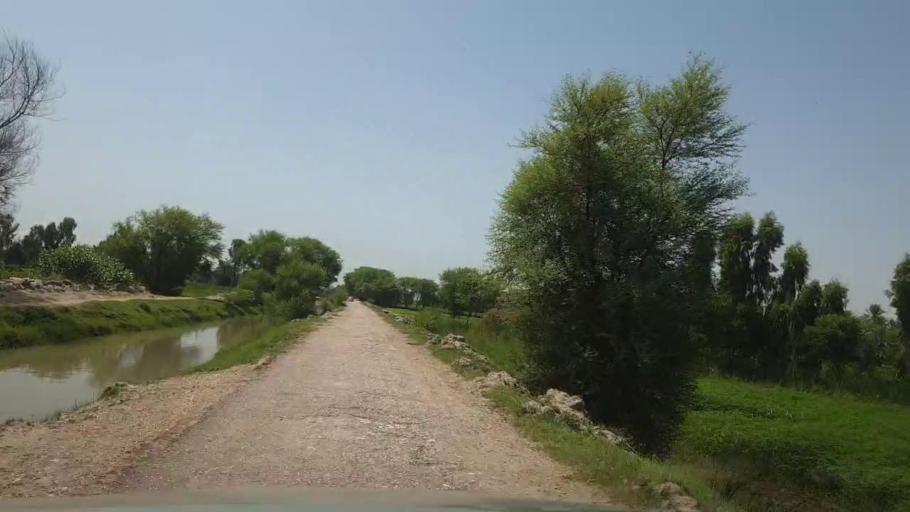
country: PK
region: Sindh
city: Rohri
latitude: 27.6555
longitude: 68.9827
